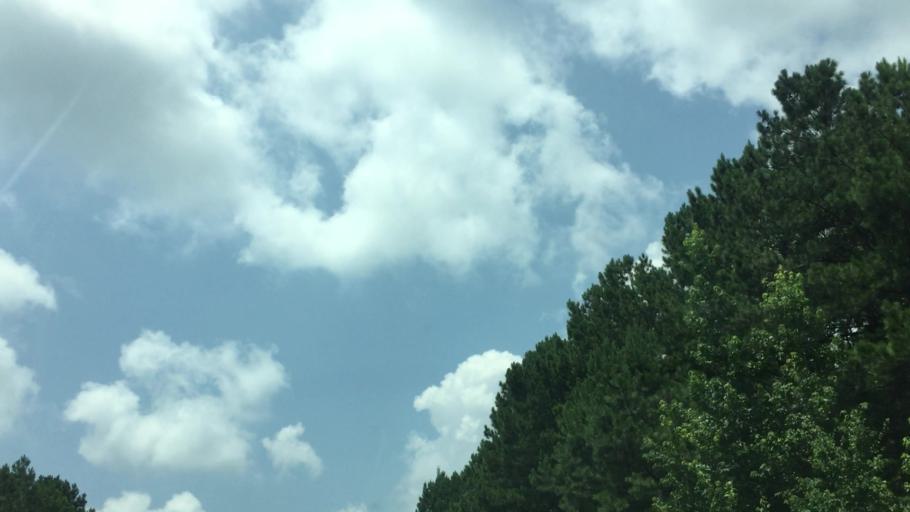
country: US
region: Georgia
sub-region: Fulton County
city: Chattahoochee Hills
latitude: 33.5637
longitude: -84.7523
